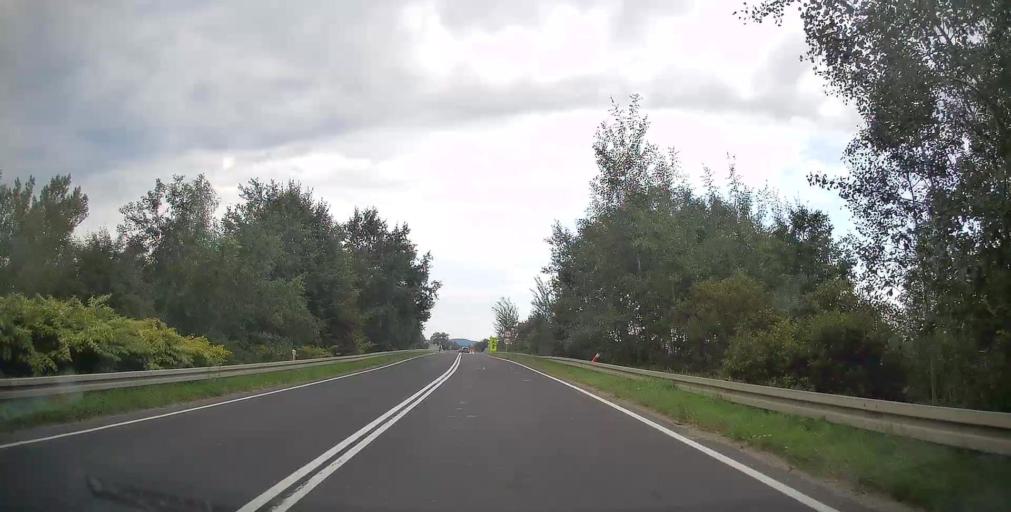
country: PL
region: Lesser Poland Voivodeship
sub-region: Powiat oswiecimski
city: Zator
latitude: 50.0282
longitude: 19.4368
